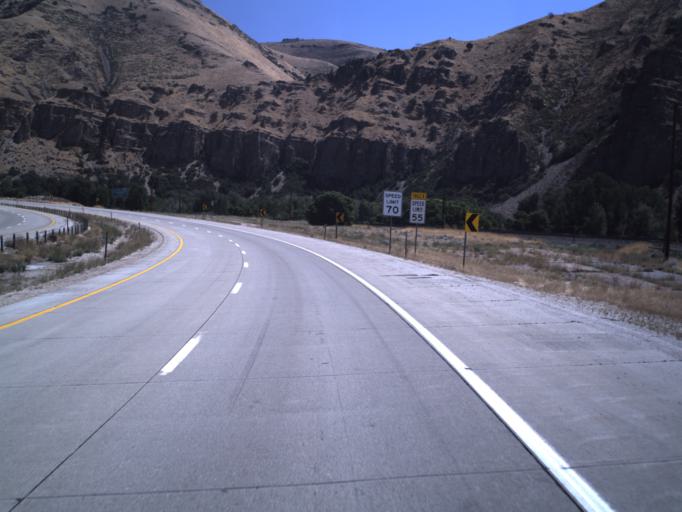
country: US
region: Utah
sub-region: Morgan County
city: Morgan
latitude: 41.0489
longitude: -111.6097
